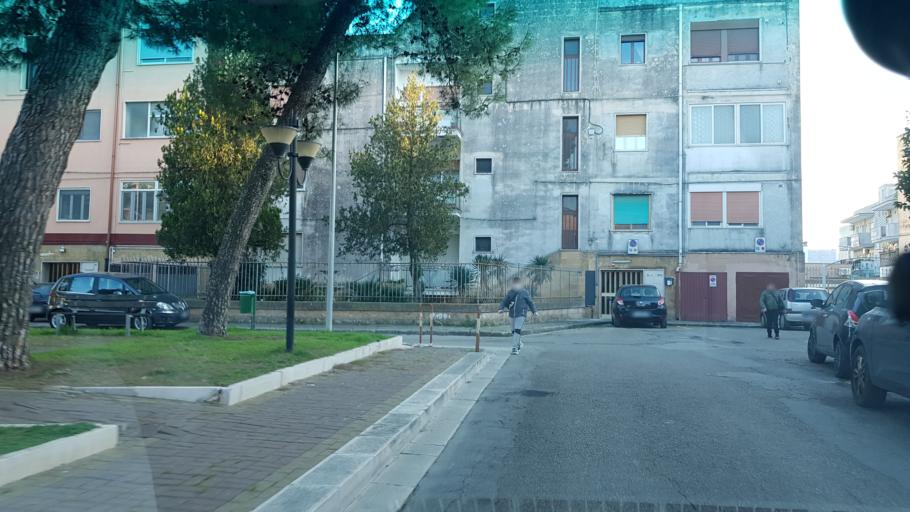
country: IT
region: Apulia
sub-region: Provincia di Brindisi
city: Mesagne
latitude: 40.5536
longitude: 17.8057
